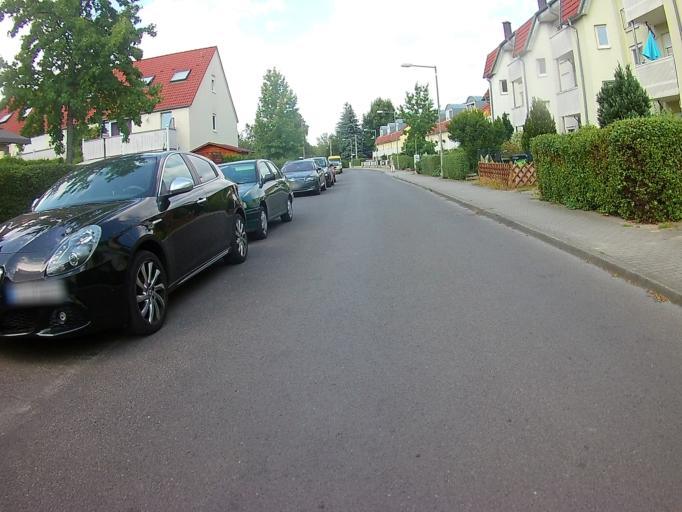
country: DE
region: Berlin
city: Bohnsdorf
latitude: 52.3977
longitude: 13.5655
